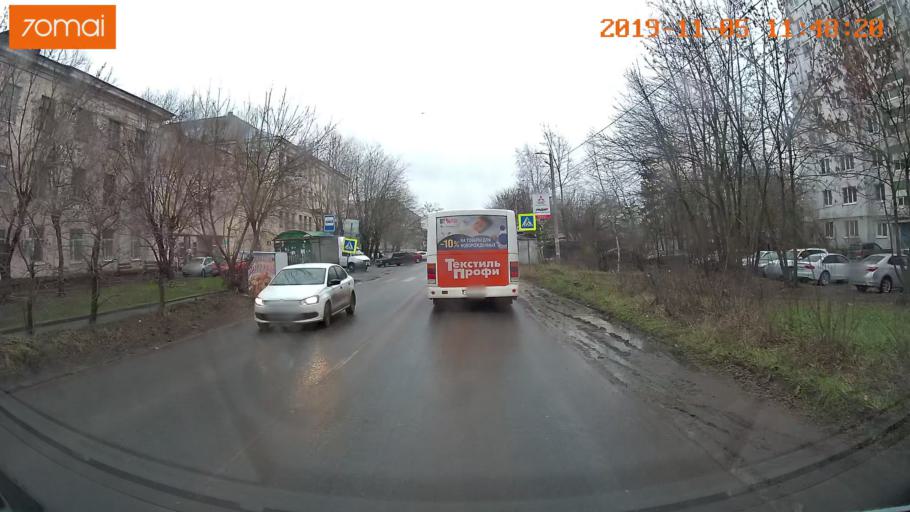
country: RU
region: Ivanovo
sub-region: Gorod Ivanovo
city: Ivanovo
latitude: 57.0089
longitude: 40.9968
